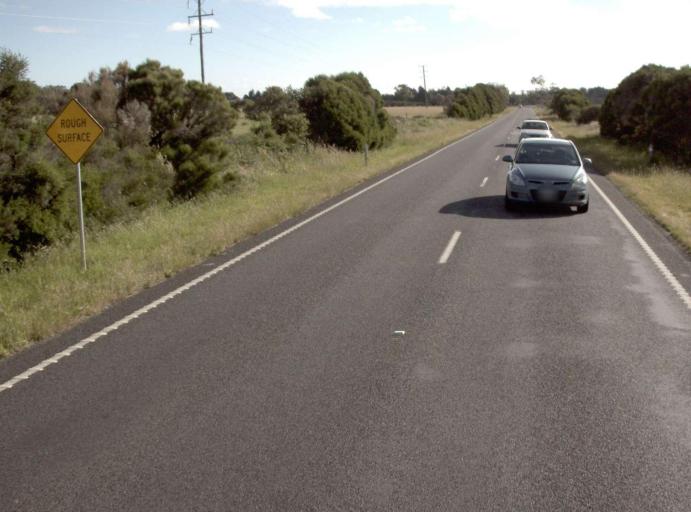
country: AU
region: Victoria
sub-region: Bass Coast
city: North Wonthaggi
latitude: -38.5740
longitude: 145.8342
